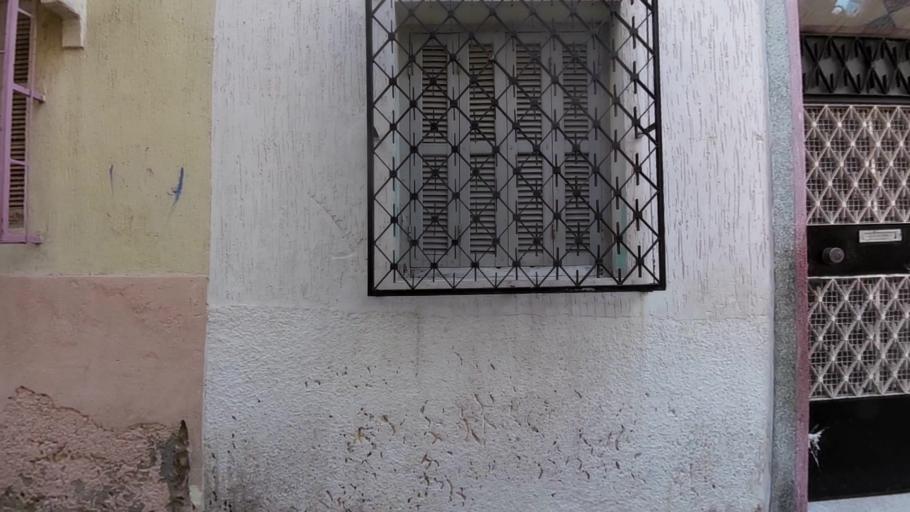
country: MA
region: Tanger-Tetouan
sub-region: Tanger-Assilah
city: Tangier
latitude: 35.7543
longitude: -5.8058
